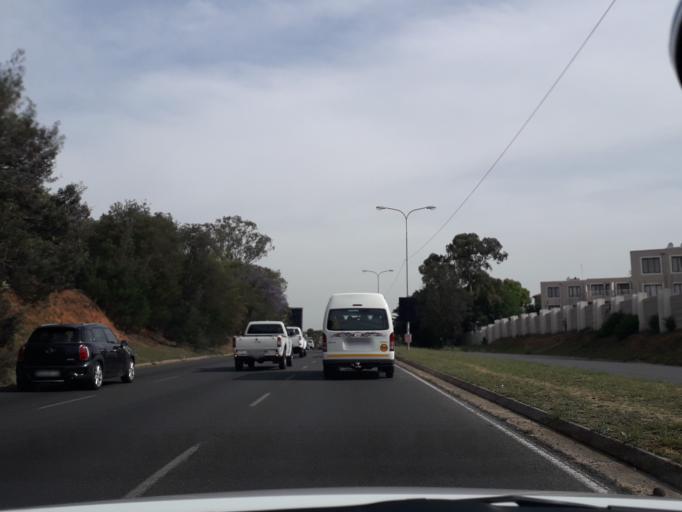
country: ZA
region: Gauteng
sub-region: City of Johannesburg Metropolitan Municipality
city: Johannesburg
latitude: -26.1131
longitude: 28.0316
